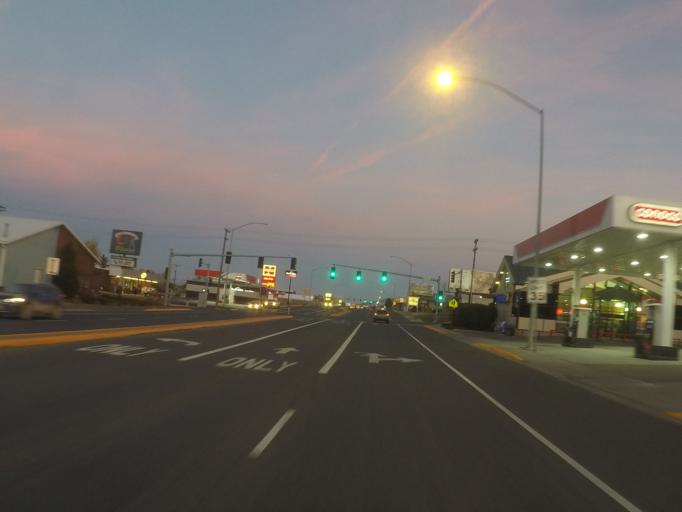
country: US
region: Montana
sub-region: Lewis and Clark County
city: Helena
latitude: 46.6035
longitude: -112.0580
